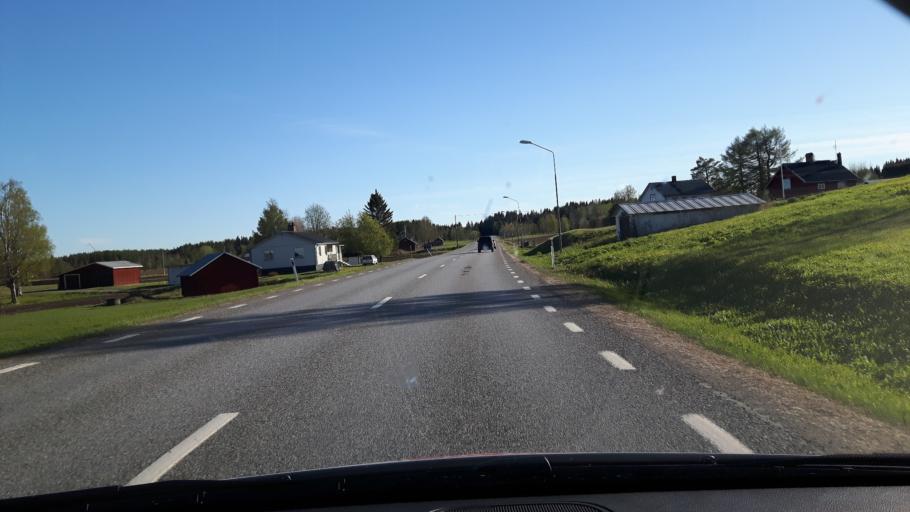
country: SE
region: Jaemtland
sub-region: Stroemsunds Kommun
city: Stroemsund
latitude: 63.4966
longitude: 15.2549
